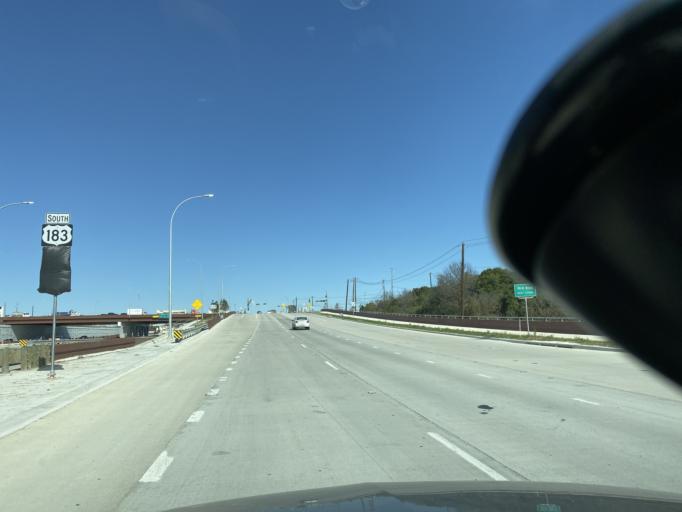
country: US
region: Texas
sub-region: Travis County
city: Austin
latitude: 30.2835
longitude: -97.6655
